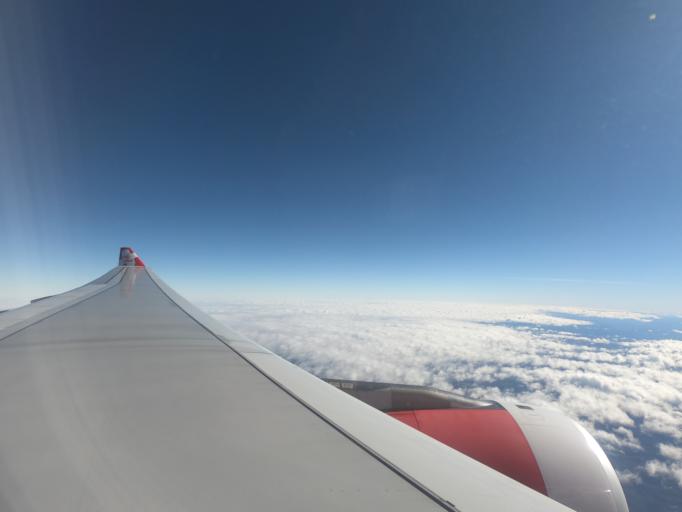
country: AU
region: New South Wales
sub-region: Goulburn Mulwaree
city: Goulburn
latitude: -34.4880
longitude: 149.9642
